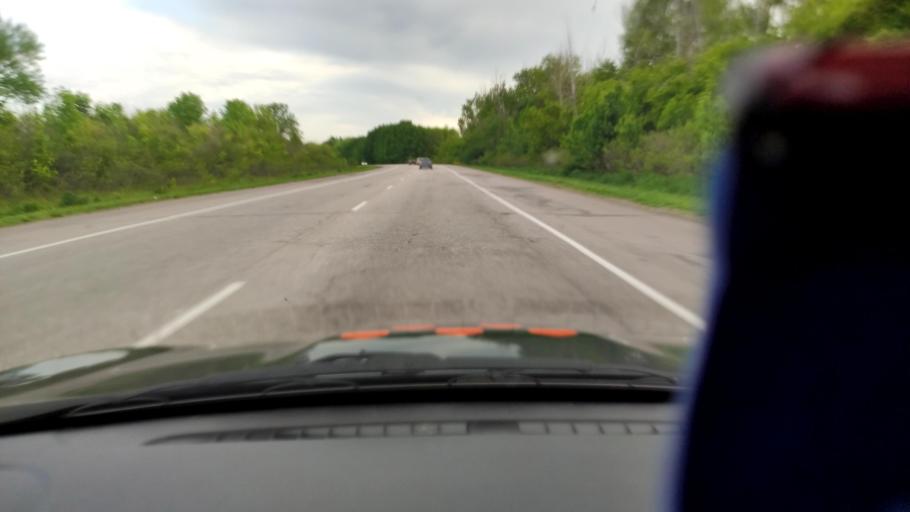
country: RU
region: Voronezj
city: Kolodeznyy
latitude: 51.2895
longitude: 39.0402
